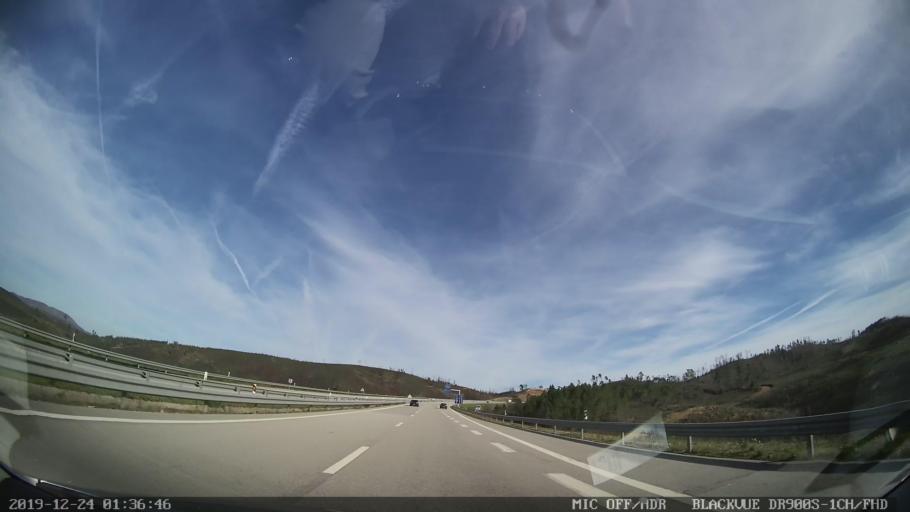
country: PT
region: Santarem
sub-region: Macao
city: Macao
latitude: 39.5231
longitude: -7.9748
